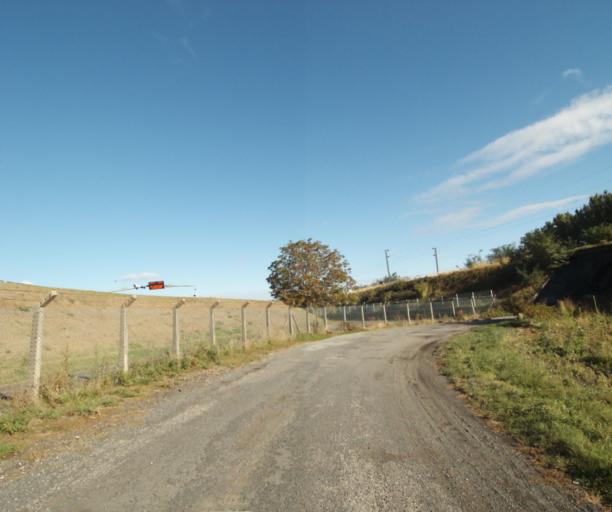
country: FR
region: Auvergne
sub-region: Departement du Puy-de-Dome
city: Gerzat
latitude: 45.8430
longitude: 3.1411
